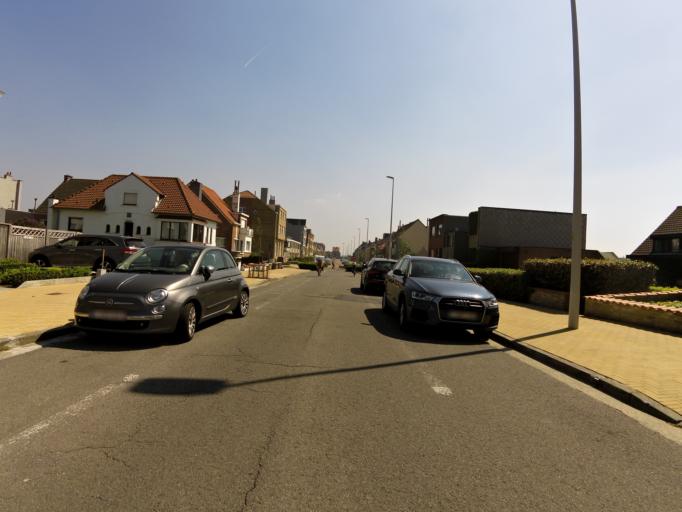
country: BE
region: Flanders
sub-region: Provincie West-Vlaanderen
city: Middelkerke
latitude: 51.2059
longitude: 2.8598
